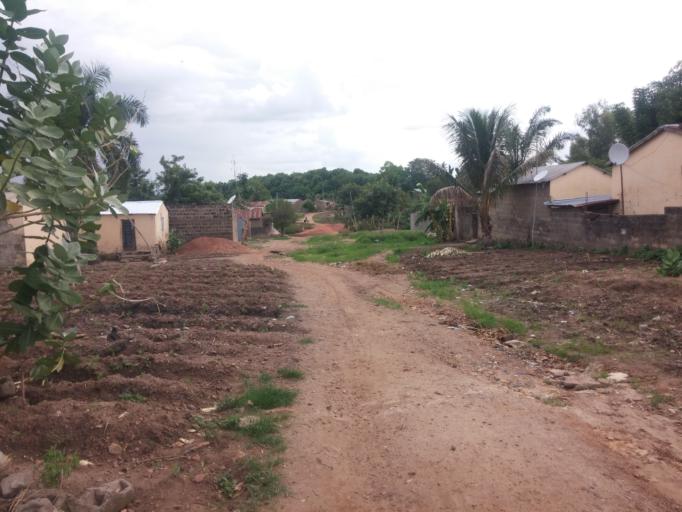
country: TG
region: Kara
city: Kara
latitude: 9.5464
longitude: 1.2047
